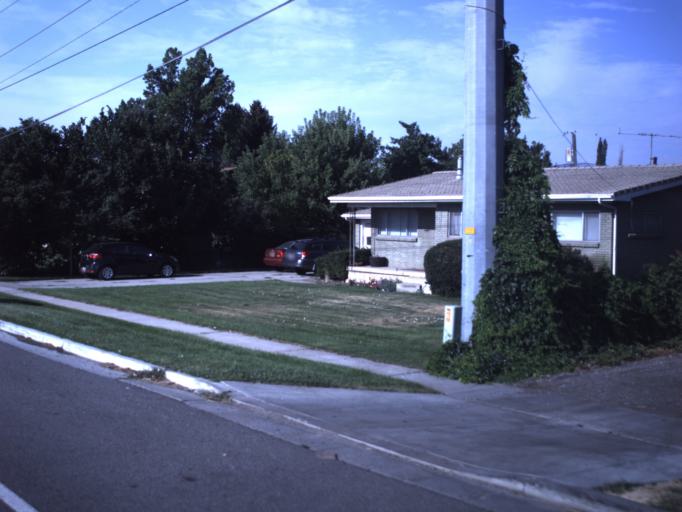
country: US
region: Utah
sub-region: Utah County
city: American Fork
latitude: 40.3710
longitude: -111.7854
